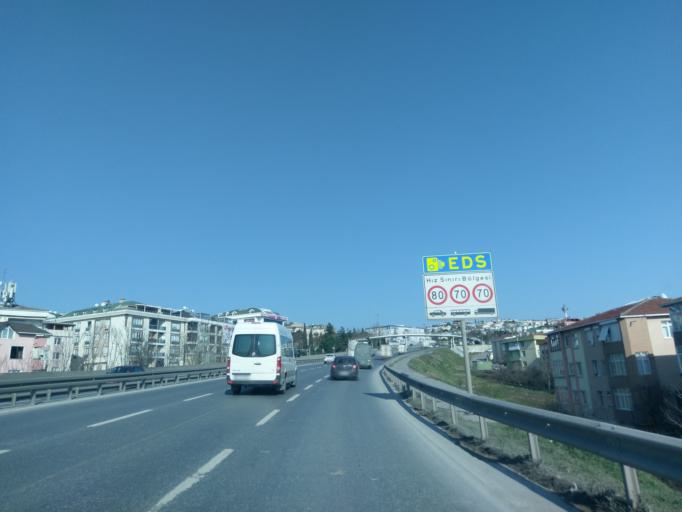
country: TR
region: Istanbul
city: Bueyuekcekmece
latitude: 41.0240
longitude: 28.5868
